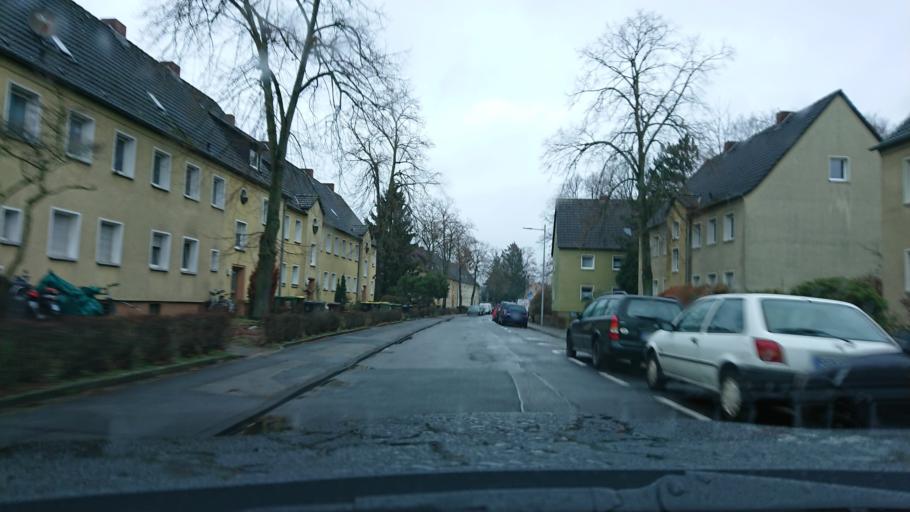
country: DE
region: North Rhine-Westphalia
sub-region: Regierungsbezirk Koln
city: Siegburg
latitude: 50.8065
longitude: 7.1893
